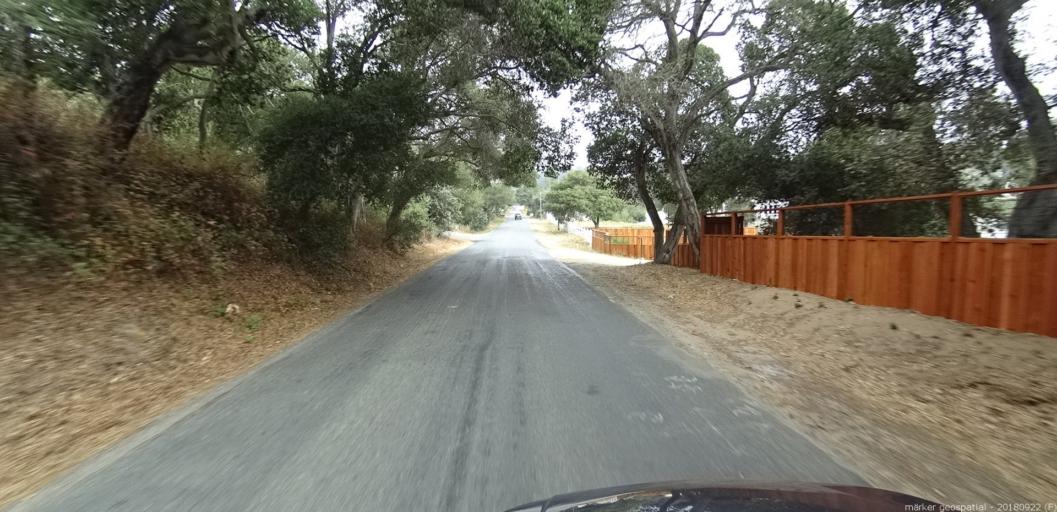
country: US
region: California
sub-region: Monterey County
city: Prunedale
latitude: 36.7841
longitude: -121.6703
